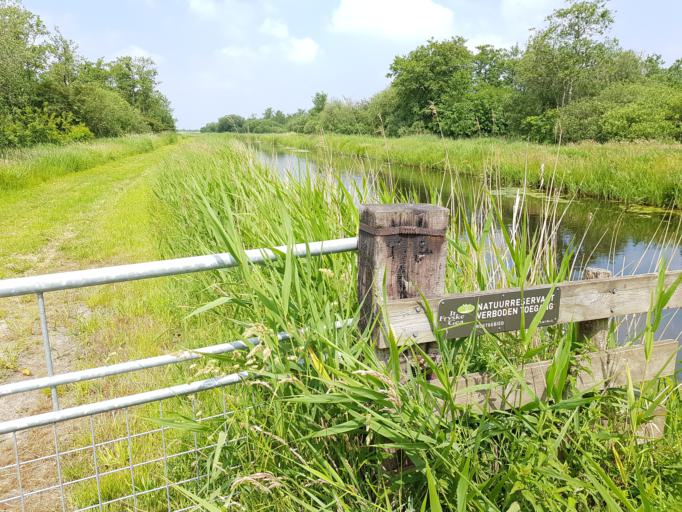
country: NL
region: Friesland
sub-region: Gemeente Boarnsterhim
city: Aldeboarn
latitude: 53.0836
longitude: 5.9164
